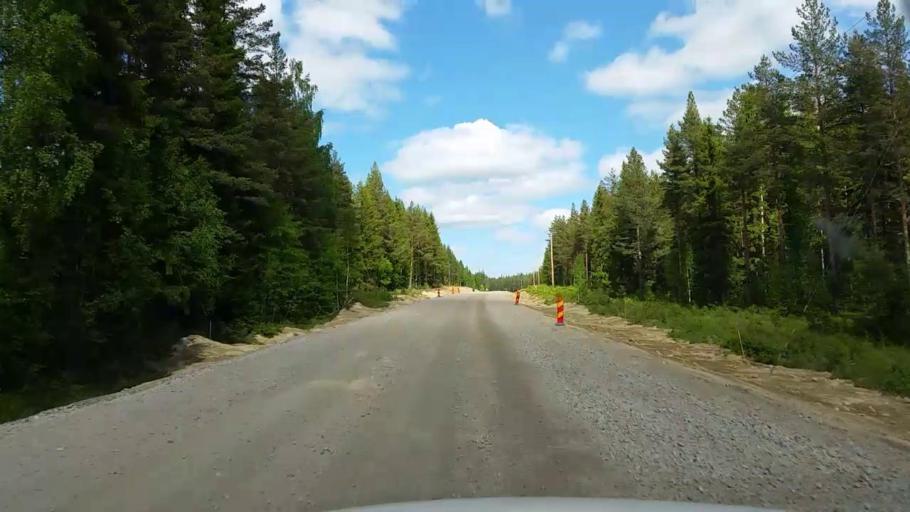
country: SE
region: Gaevleborg
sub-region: Ovanakers Kommun
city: Edsbyn
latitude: 61.5837
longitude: 15.9070
